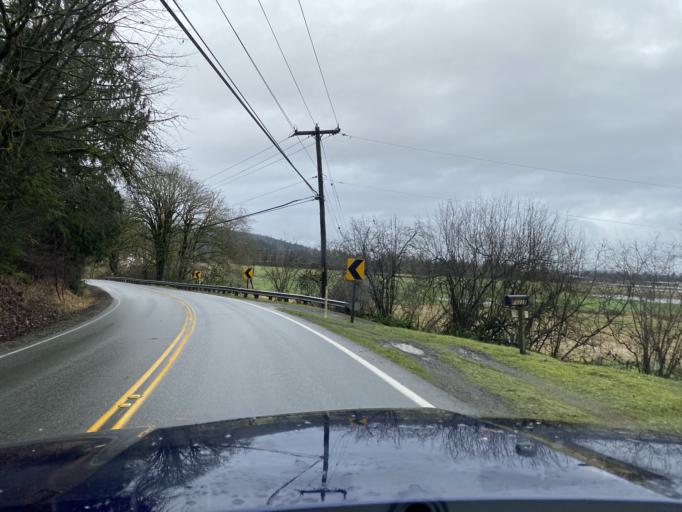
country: US
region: Washington
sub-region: King County
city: Duvall
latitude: 47.7290
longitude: -122.0103
